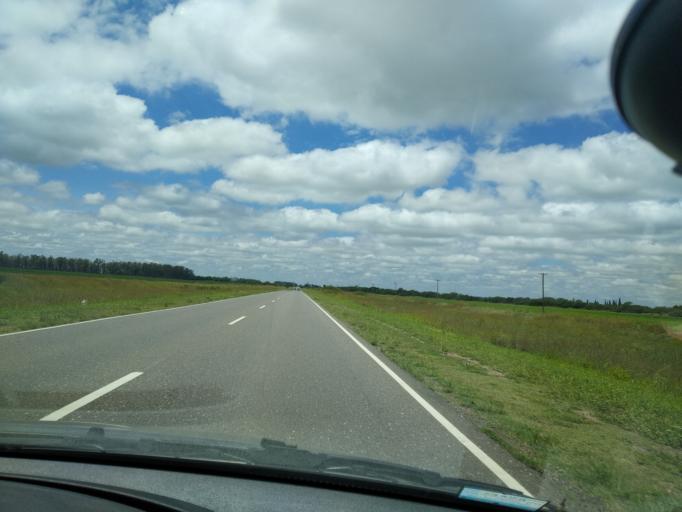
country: AR
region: Cordoba
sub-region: Departamento de Rio Segundo
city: Rio Segundo
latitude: -31.6432
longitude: -63.9583
